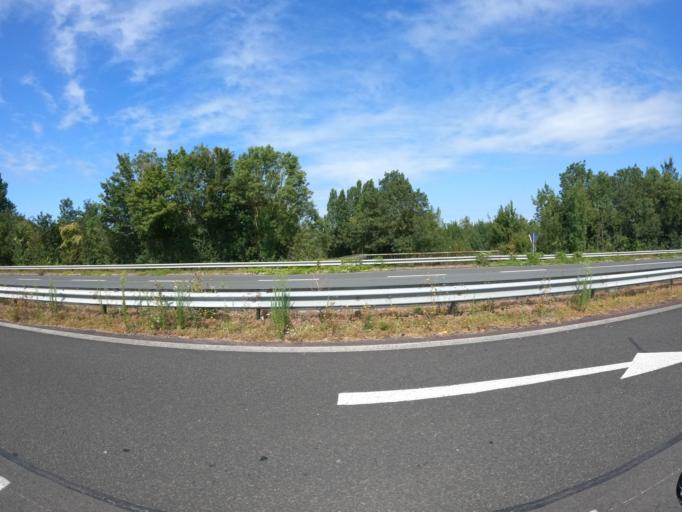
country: FR
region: Poitou-Charentes
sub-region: Departement des Deux-Sevres
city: Frontenay-Rohan-Rohan
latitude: 46.2600
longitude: -0.5383
